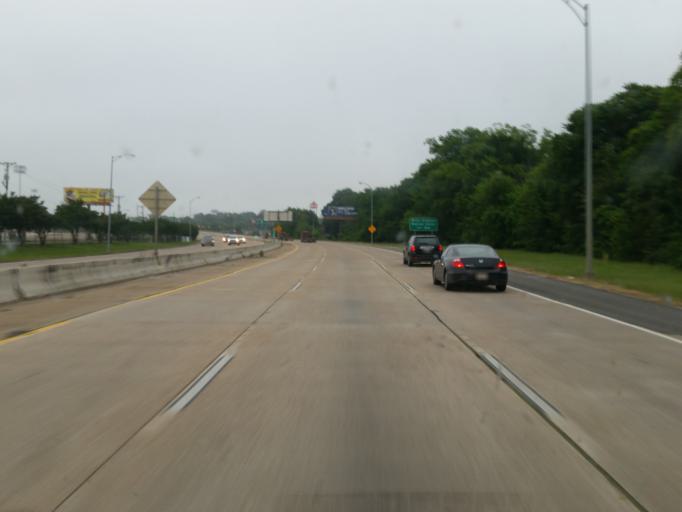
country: US
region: Louisiana
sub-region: Caddo Parish
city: Shreveport
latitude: 32.4755
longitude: -93.7859
